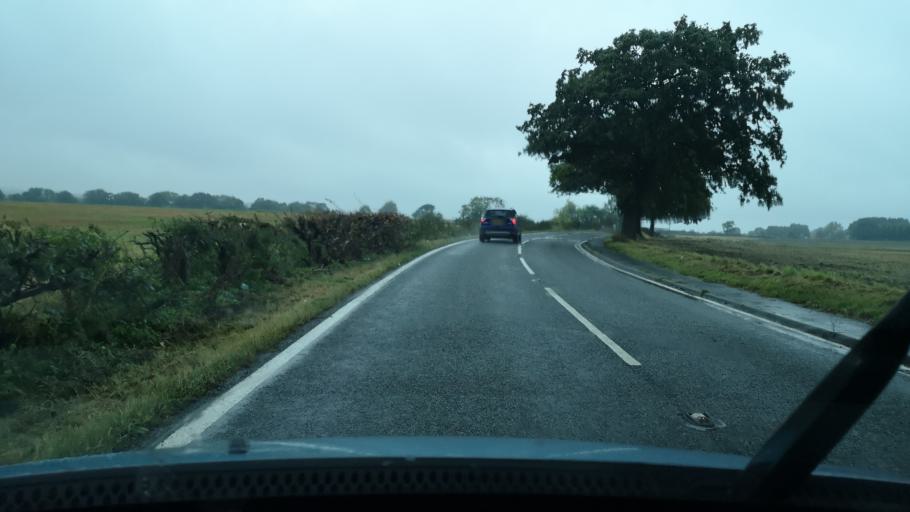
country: GB
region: England
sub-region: City and Borough of Wakefield
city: Featherstone
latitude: 53.6643
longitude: -1.3485
